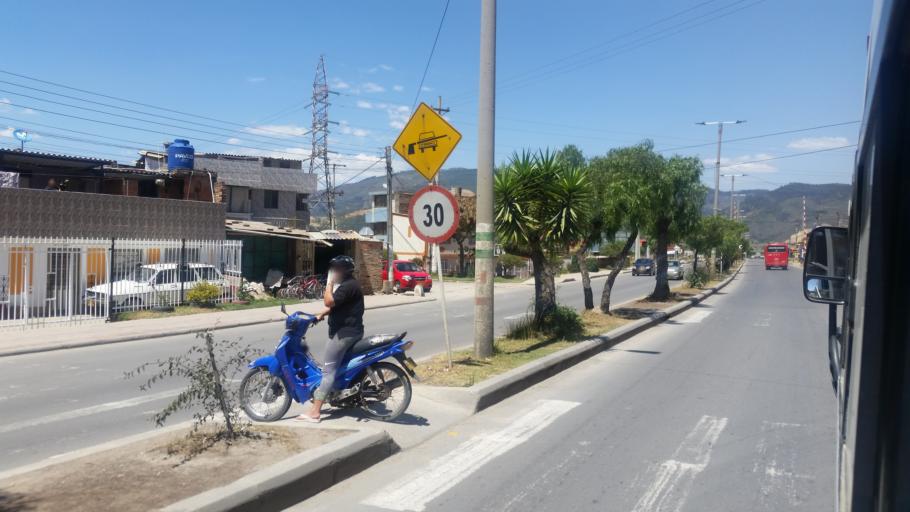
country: CO
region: Boyaca
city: Sogamoso
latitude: 5.7420
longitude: -72.9150
